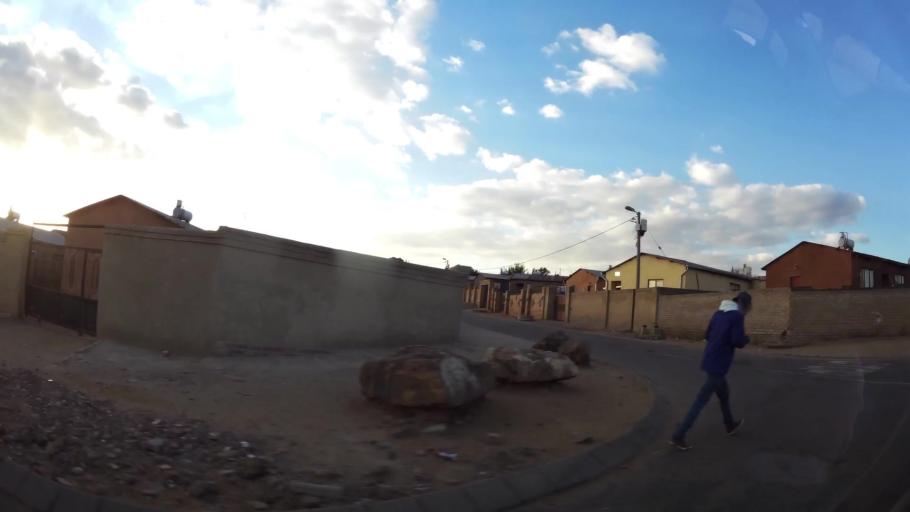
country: ZA
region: Gauteng
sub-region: West Rand District Municipality
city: Krugersdorp
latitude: -26.0769
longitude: 27.7489
